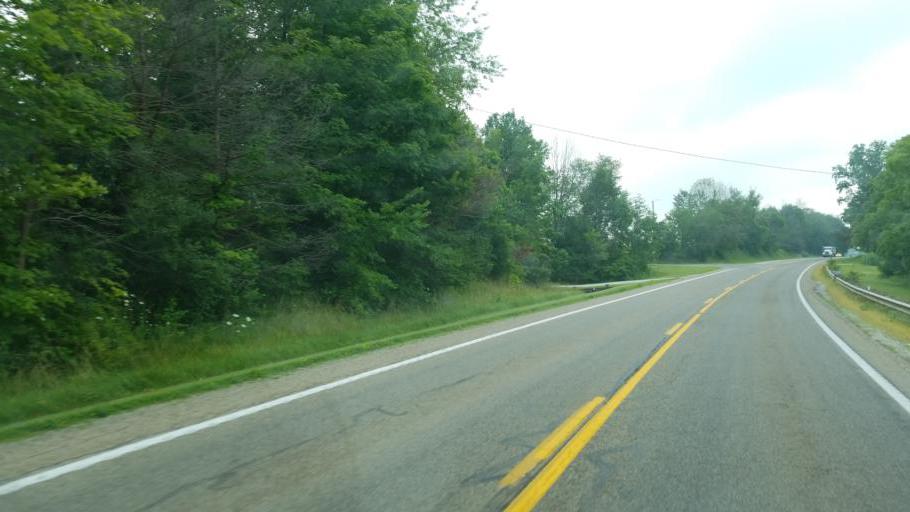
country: US
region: Ohio
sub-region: Morrow County
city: Mount Gilead
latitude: 40.5459
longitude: -82.7980
